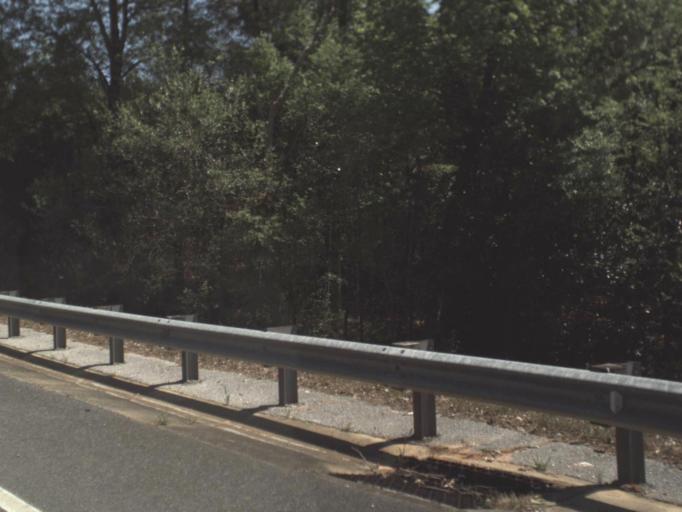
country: US
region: Florida
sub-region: Escambia County
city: Century
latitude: 30.9488
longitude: -87.1860
